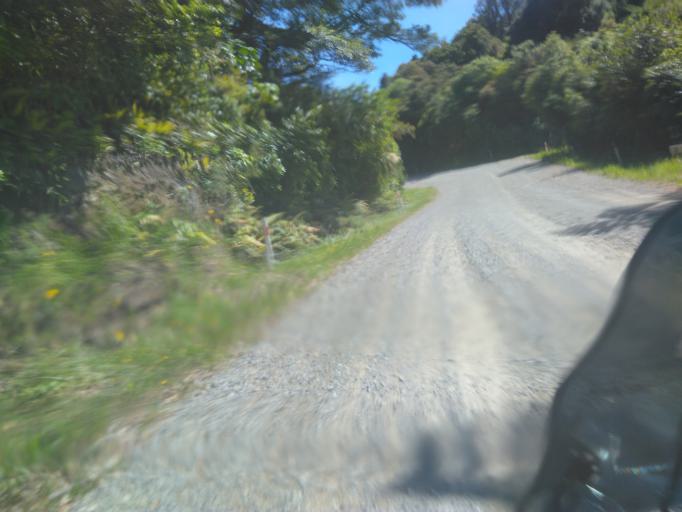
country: NZ
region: Hawke's Bay
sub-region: Wairoa District
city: Wairoa
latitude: -38.7957
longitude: 177.1247
